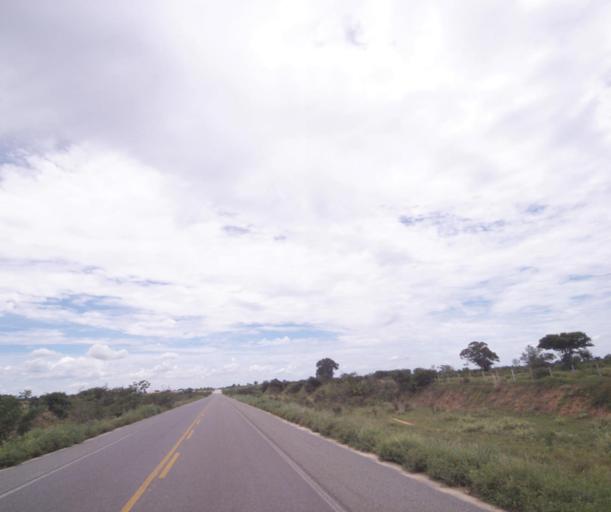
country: BR
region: Bahia
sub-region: Carinhanha
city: Carinhanha
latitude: -14.2921
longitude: -43.7856
